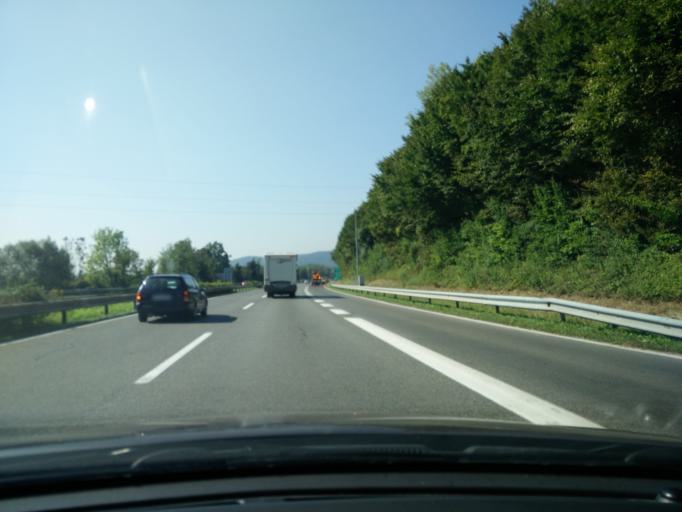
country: SI
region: Medvode
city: Zgornje Pirnice
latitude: 46.1219
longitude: 14.4804
